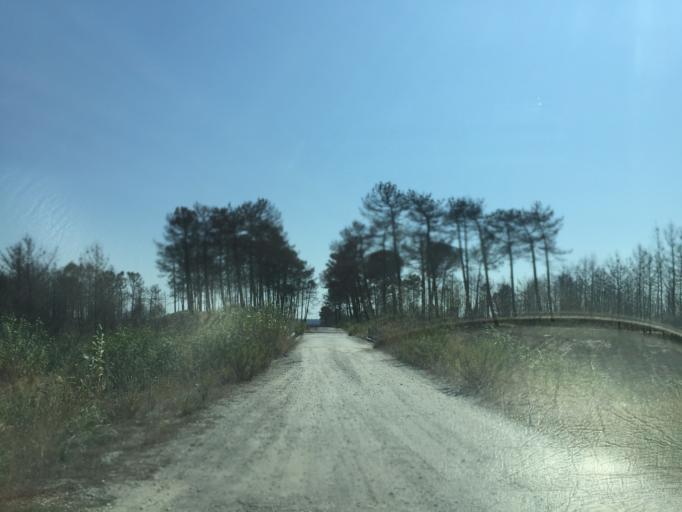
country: PT
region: Coimbra
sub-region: Figueira da Foz
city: Alhadas
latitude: 40.2654
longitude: -8.8326
